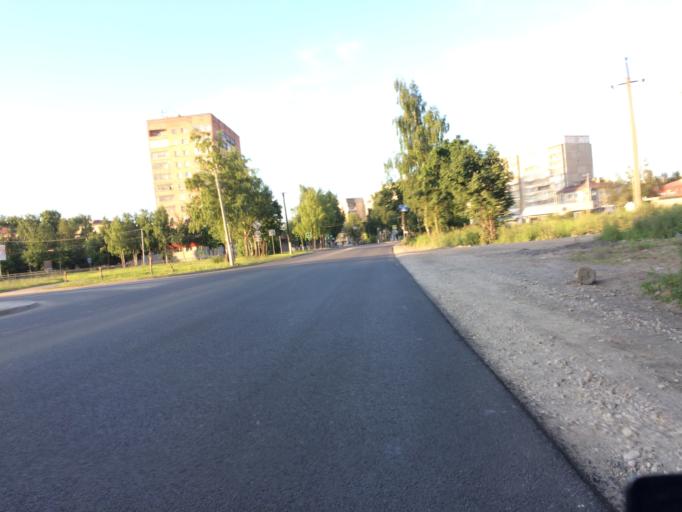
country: RU
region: Mariy-El
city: Medvedevo
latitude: 56.6415
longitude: 47.8314
